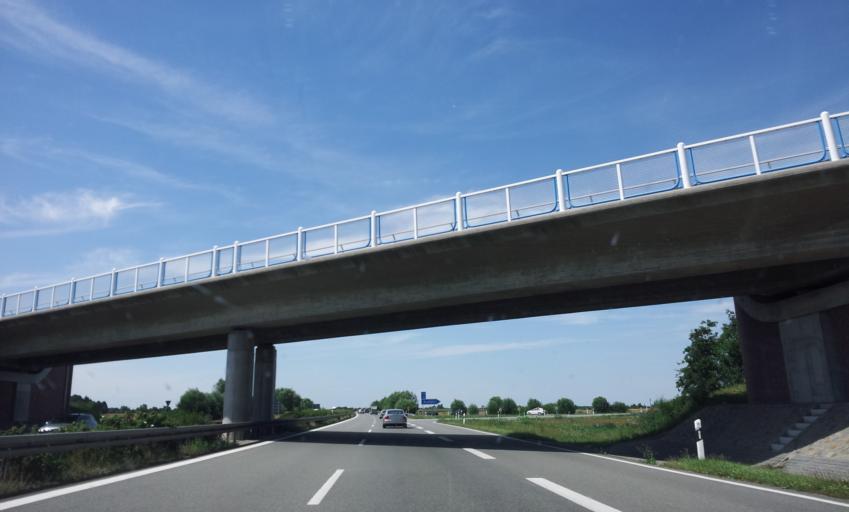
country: DE
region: Mecklenburg-Vorpommern
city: Dersekow
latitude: 54.0717
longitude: 13.2114
